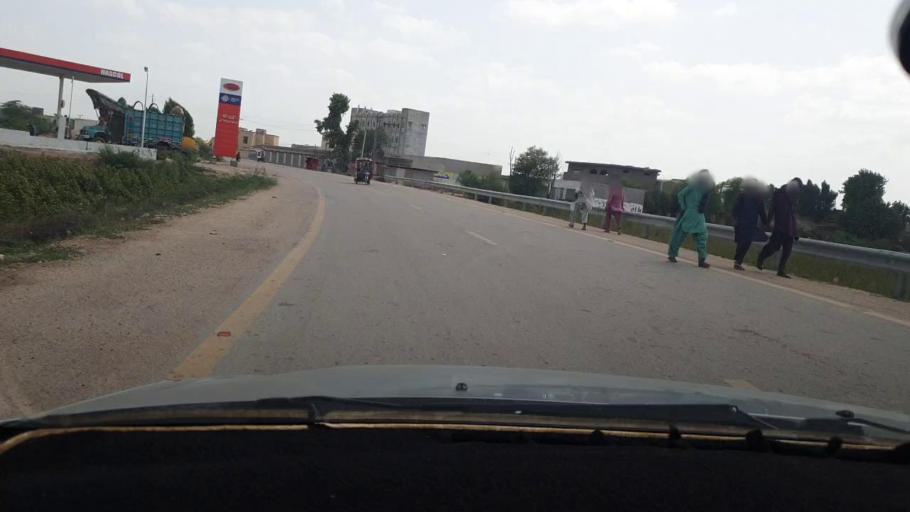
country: PK
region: Sindh
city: Digri
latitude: 25.0605
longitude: 69.2178
